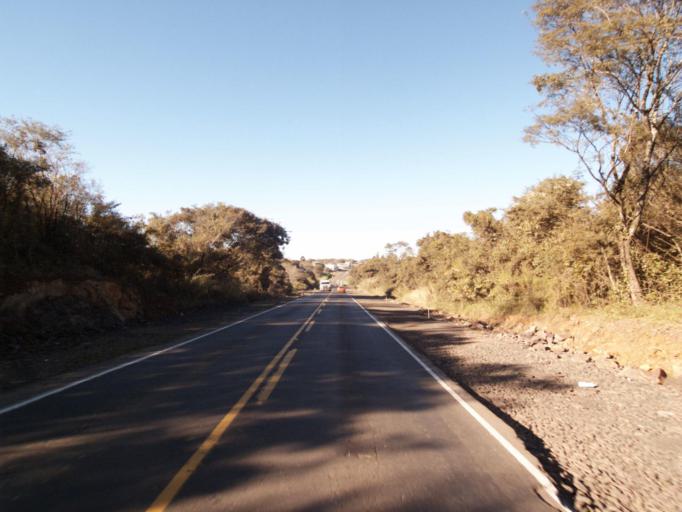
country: AR
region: Misiones
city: Bernardo de Irigoyen
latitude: -26.6517
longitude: -53.5182
